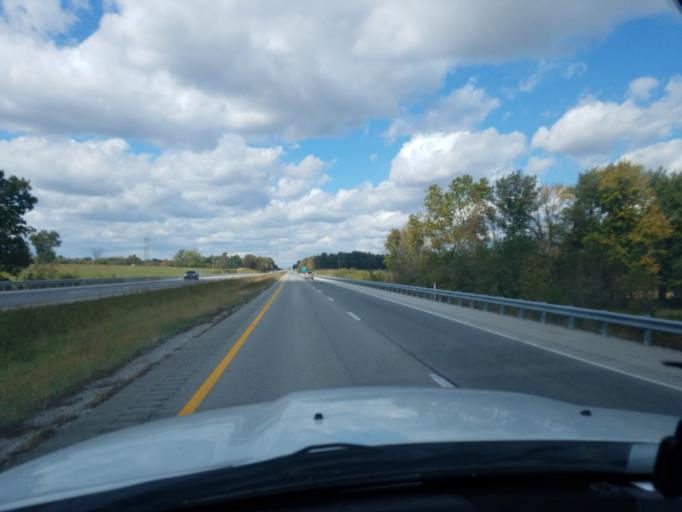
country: US
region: Kentucky
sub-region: Daviess County
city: Masonville
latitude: 37.7211
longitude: -87.0541
